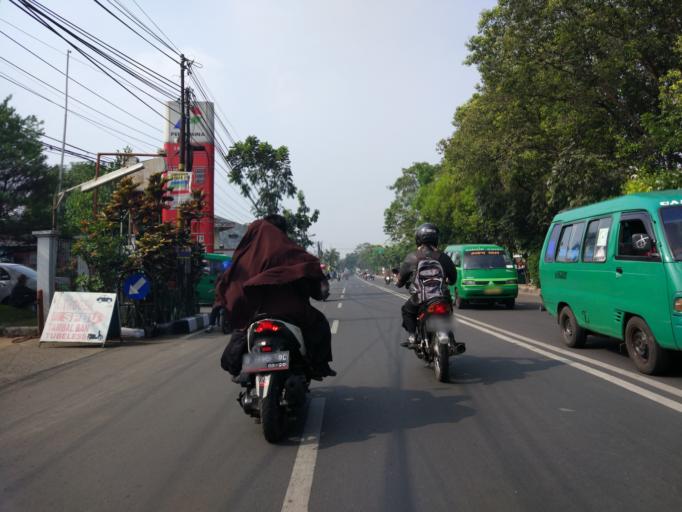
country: ID
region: West Java
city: Cileunyi
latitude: -6.9290
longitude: 107.7118
